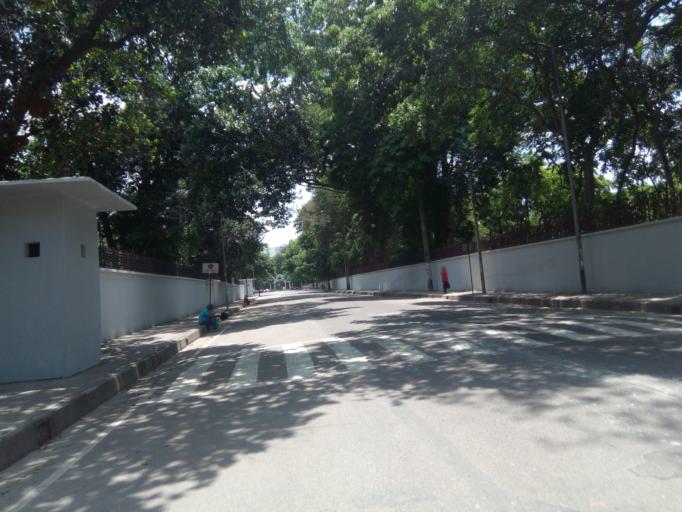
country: BD
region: Dhaka
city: Paltan
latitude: 23.7409
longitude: 90.4026
